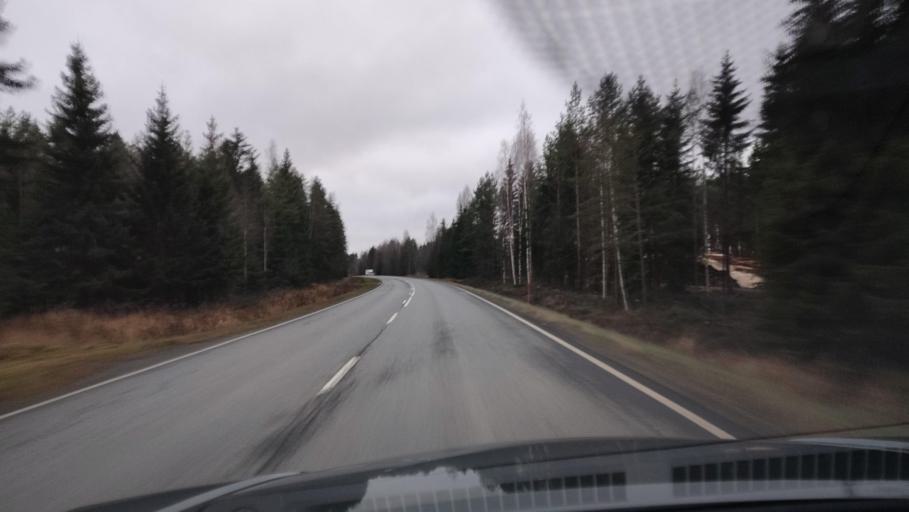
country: FI
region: Southern Ostrobothnia
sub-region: Suupohja
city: Kauhajoki
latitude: 62.3916
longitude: 22.1484
